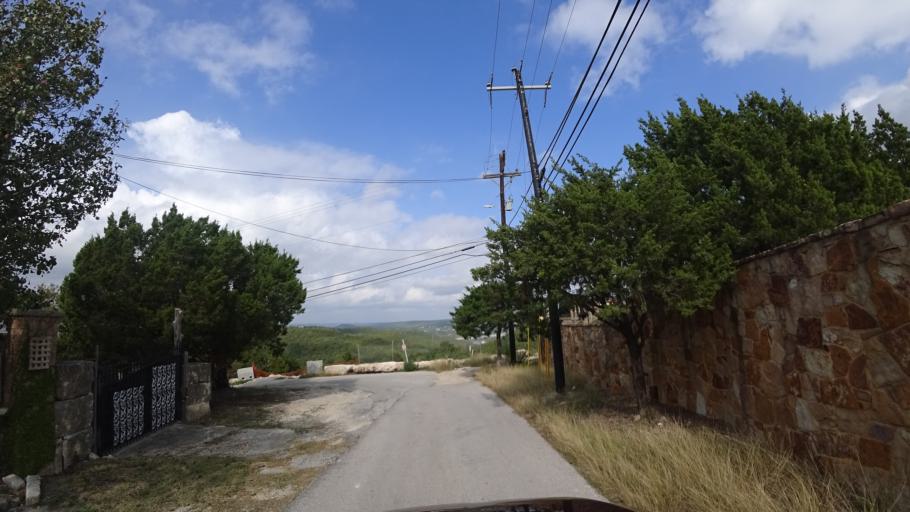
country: US
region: Texas
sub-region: Travis County
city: Hudson Bend
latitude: 30.4119
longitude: -97.8753
